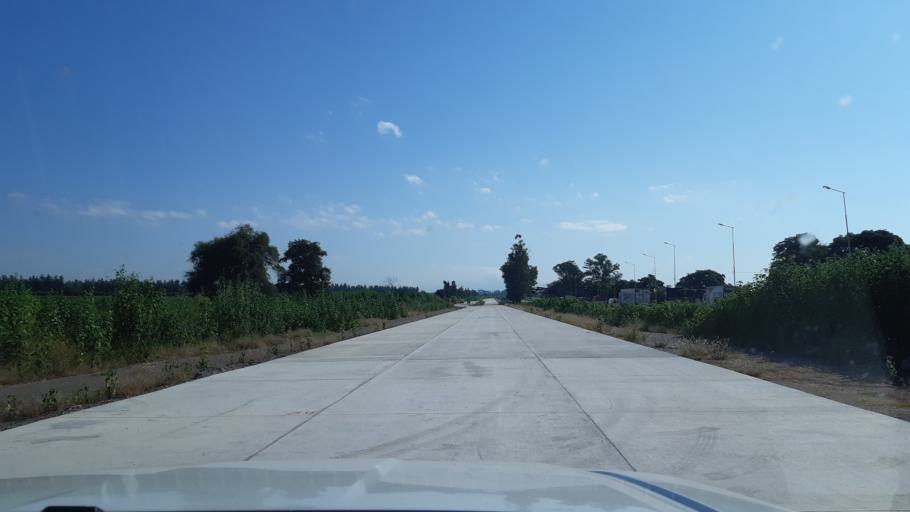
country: AR
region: Salta
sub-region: Departamento de General Guemes
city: General Martin Miguel de Guemes
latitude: -24.5601
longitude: -65.0790
